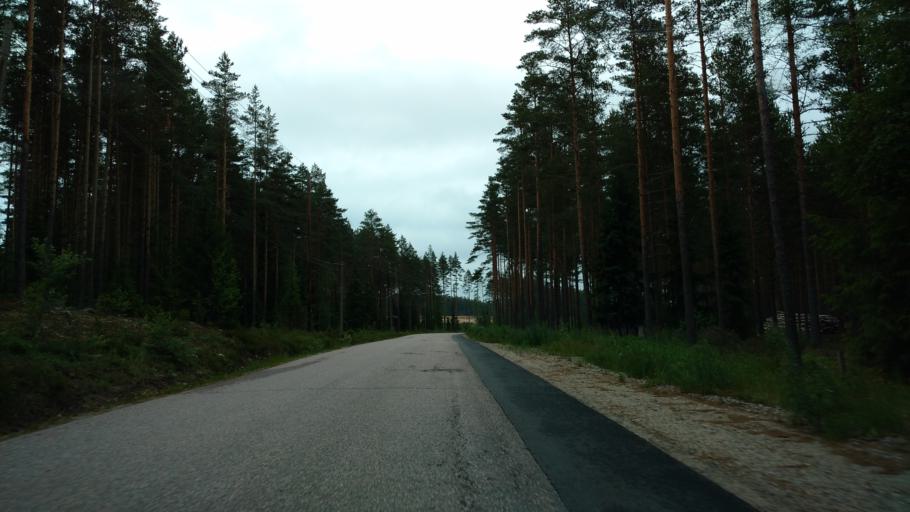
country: FI
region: Varsinais-Suomi
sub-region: Salo
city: Kiikala
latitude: 60.4328
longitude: 23.6005
